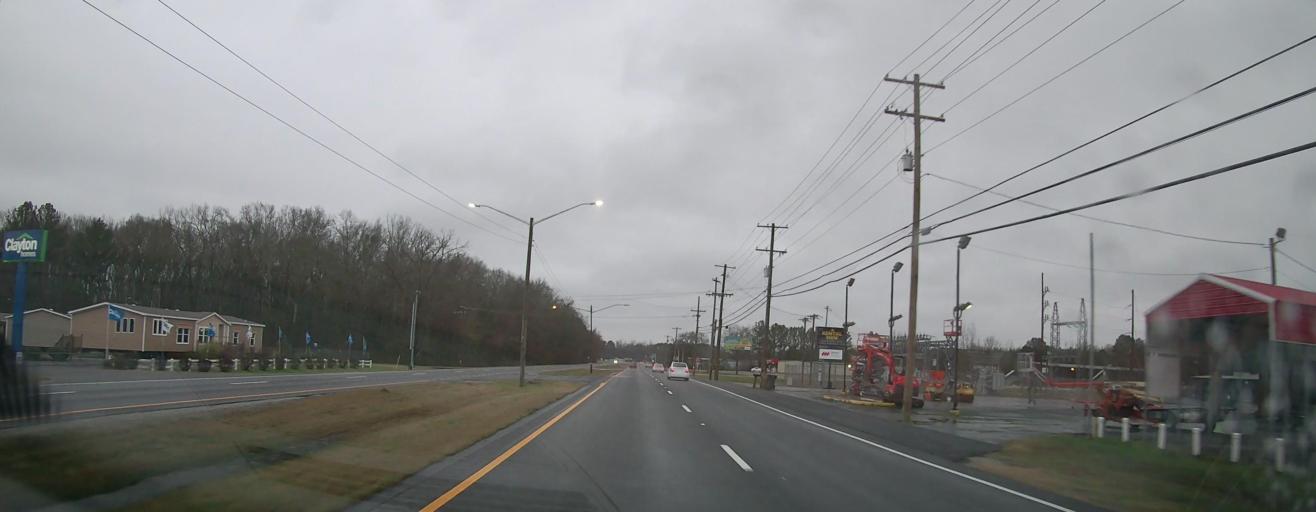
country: US
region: Alabama
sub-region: Morgan County
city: Flint City
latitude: 34.5389
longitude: -86.9739
